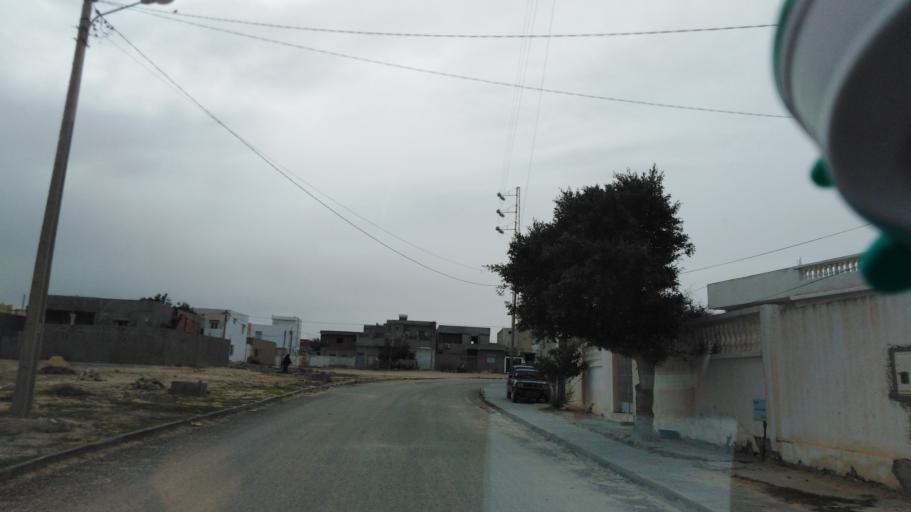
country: TN
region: Qabis
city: Gabes
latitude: 33.9535
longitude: 10.0040
